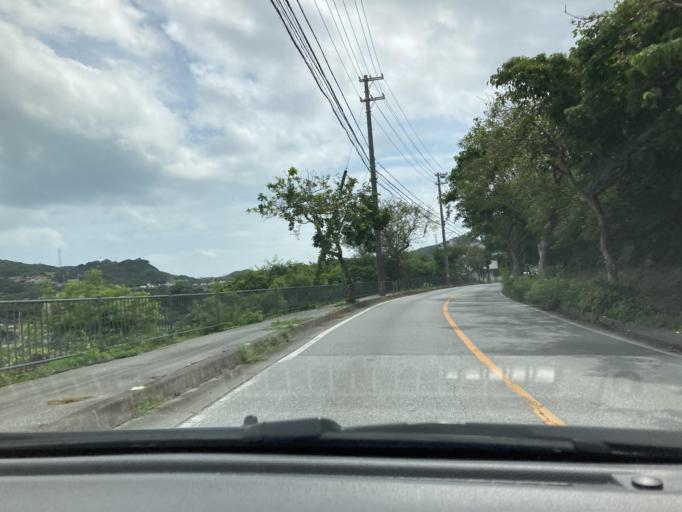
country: JP
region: Okinawa
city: Chatan
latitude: 26.2886
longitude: 127.7864
